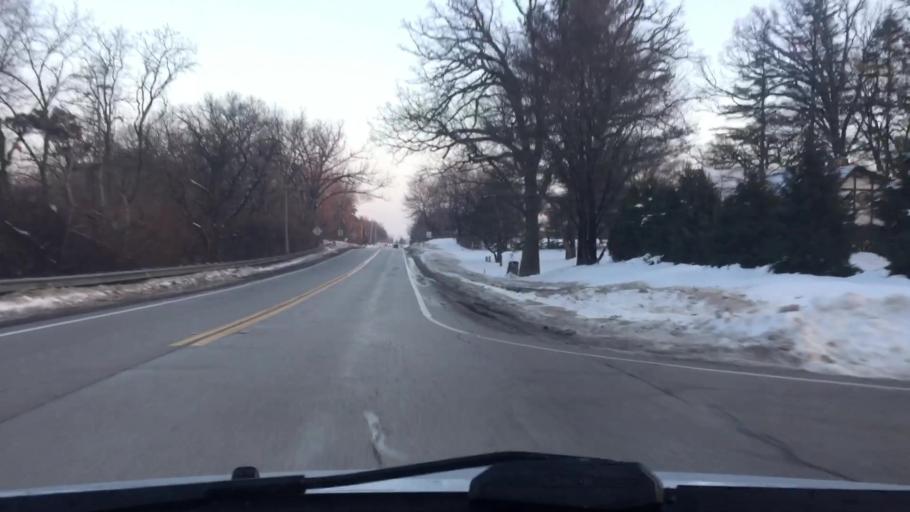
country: US
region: Illinois
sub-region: Kane County
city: Wasco
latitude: 41.9490
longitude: -88.4070
